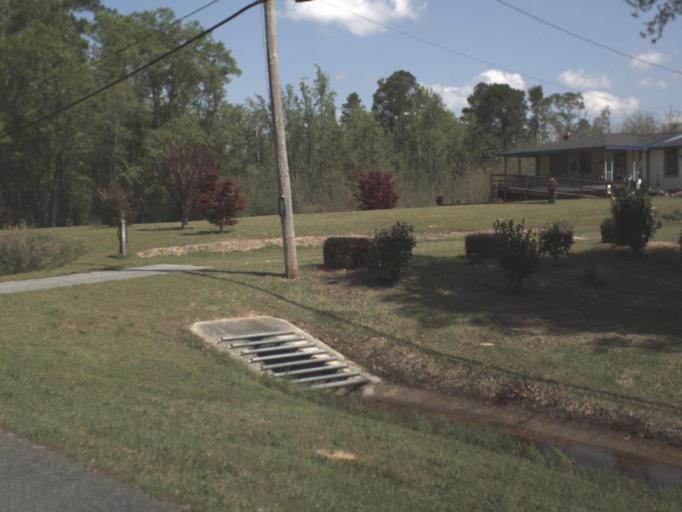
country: US
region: Alabama
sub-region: Escambia County
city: East Brewton
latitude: 30.9199
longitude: -87.0471
